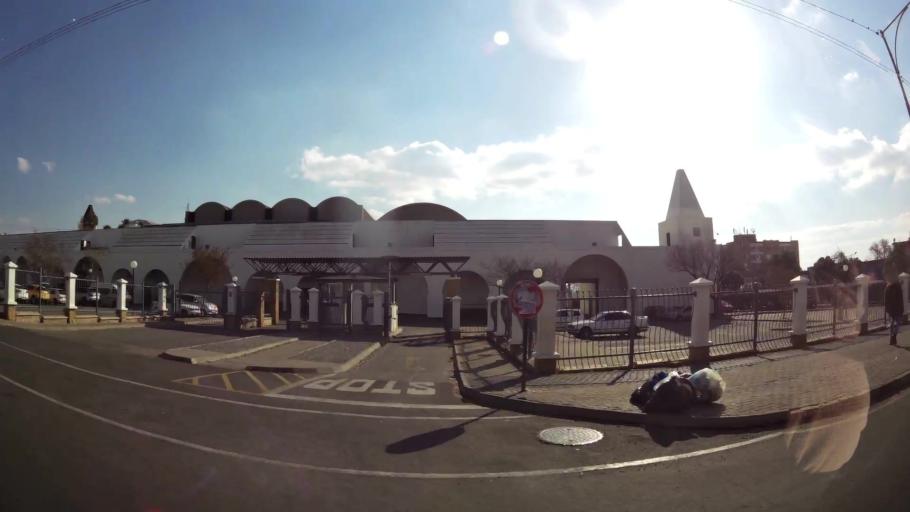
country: ZA
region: Gauteng
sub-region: West Rand District Municipality
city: Krugersdorp
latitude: -26.1005
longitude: 27.7739
